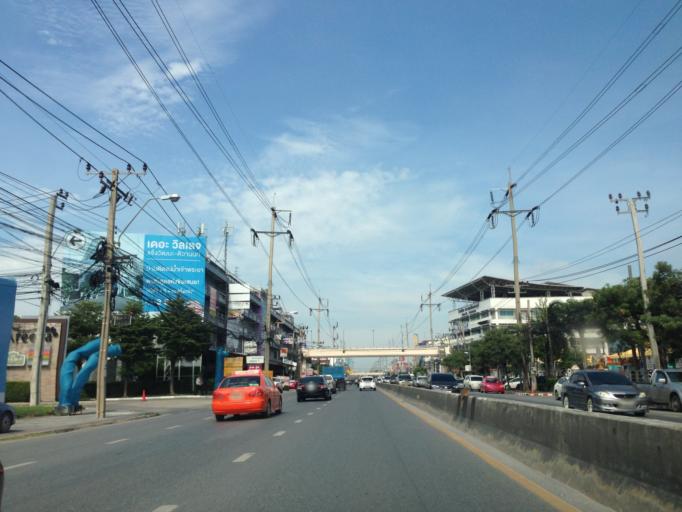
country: TH
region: Phra Nakhon Si Ayutthaya
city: Ban Bang Kadi Pathum Thani
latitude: 13.9471
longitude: 100.5455
